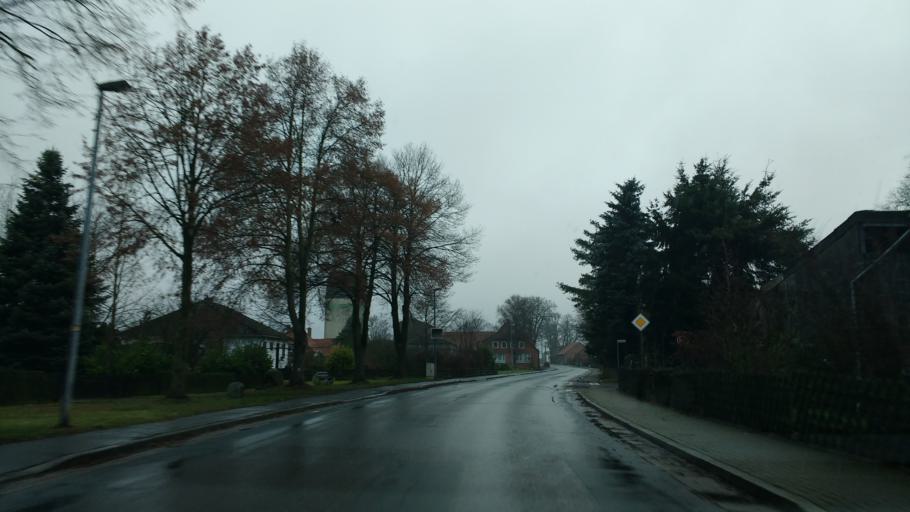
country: DE
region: Lower Saxony
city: Schwarmstedt
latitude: 52.6452
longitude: 9.5733
